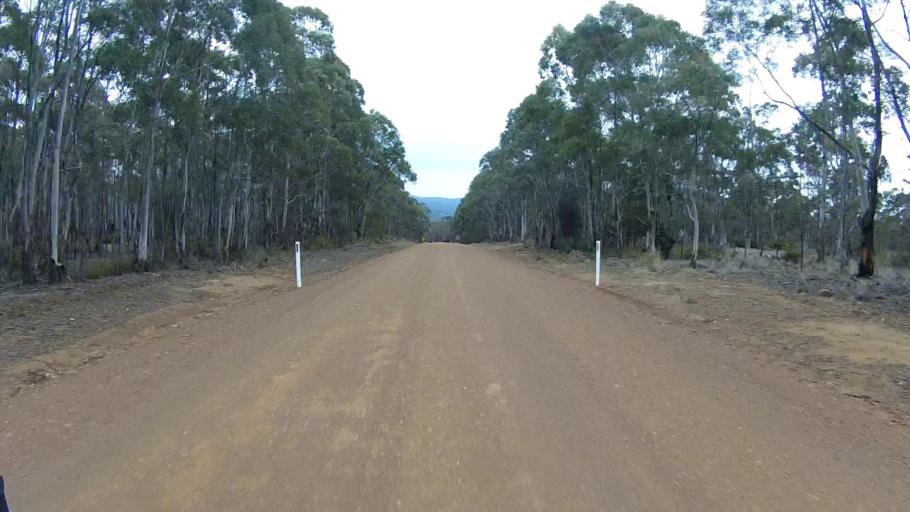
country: AU
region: Tasmania
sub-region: Sorell
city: Sorell
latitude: -42.5813
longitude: 147.8809
